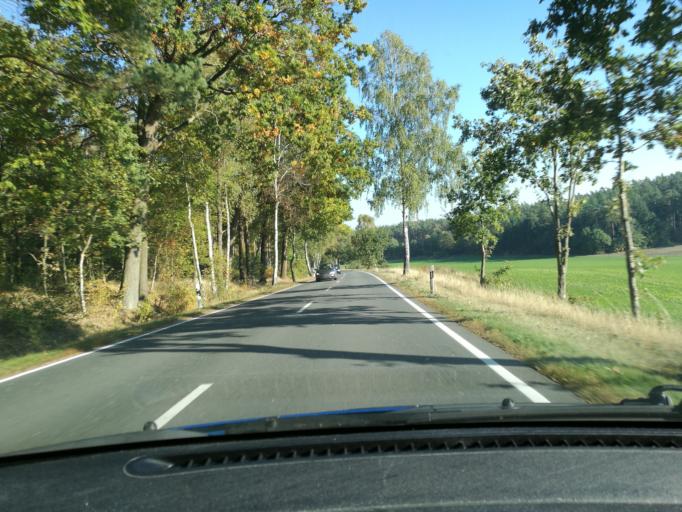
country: DE
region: Lower Saxony
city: Gohrde
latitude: 53.1271
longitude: 10.9264
